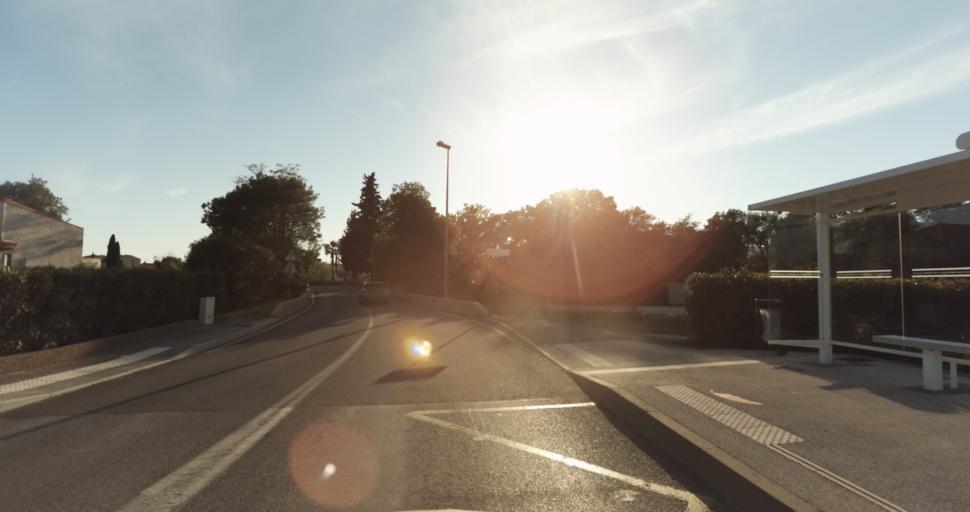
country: FR
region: Provence-Alpes-Cote d'Azur
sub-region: Departement du Var
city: La Crau
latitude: 43.1516
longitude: 6.0822
